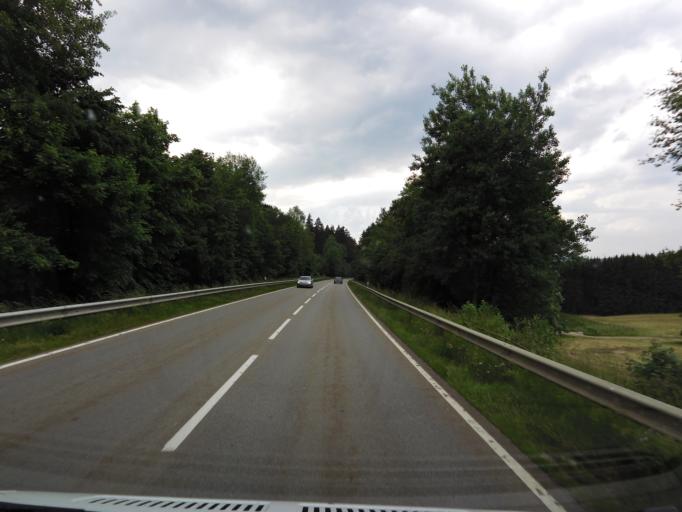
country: DE
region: Bavaria
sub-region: Lower Bavaria
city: Hutthurm
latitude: 48.6785
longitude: 13.4802
